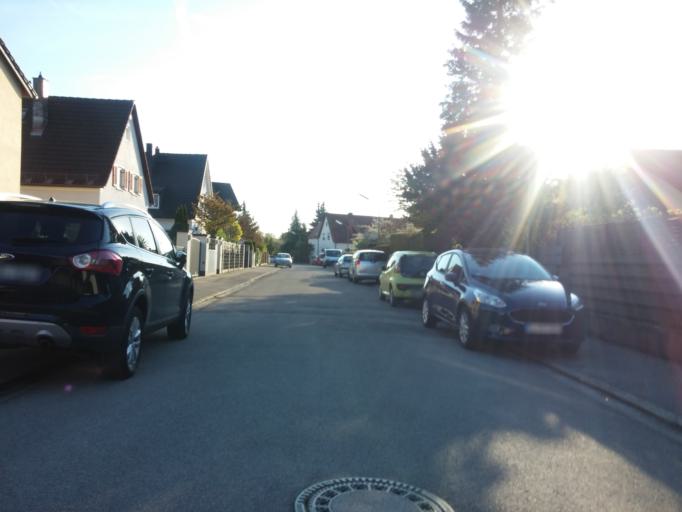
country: DE
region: Bavaria
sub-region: Upper Bavaria
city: Neubiberg
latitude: 48.1141
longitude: 11.6745
